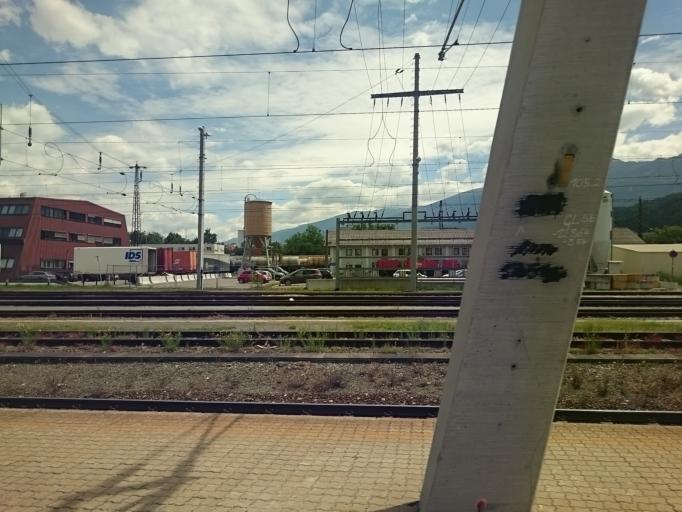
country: AT
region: Tyrol
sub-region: Innsbruck Stadt
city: Innsbruck
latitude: 47.2605
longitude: 11.4005
